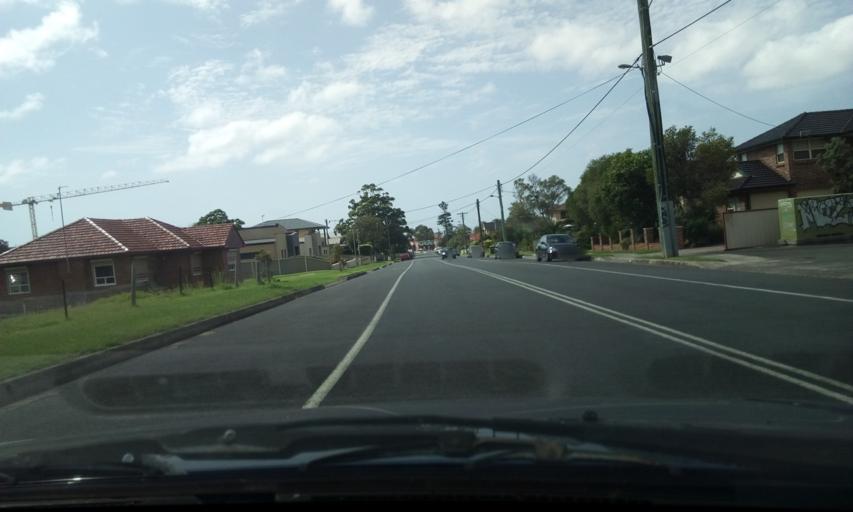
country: AU
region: New South Wales
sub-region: Wollongong
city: Corrimal
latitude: -34.3706
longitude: 150.8934
